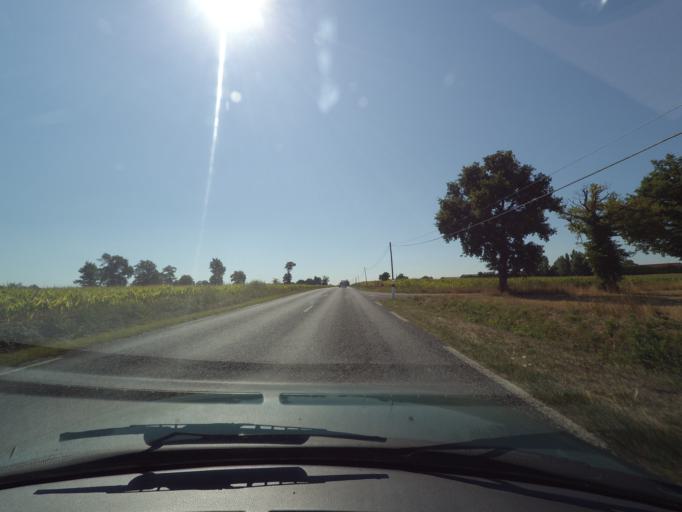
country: FR
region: Limousin
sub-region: Departement de la Haute-Vienne
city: Bellac
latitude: 46.0779
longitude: 1.0942
